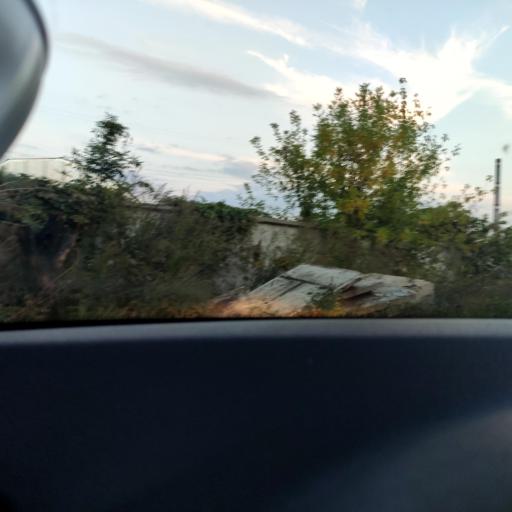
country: RU
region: Samara
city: Petra-Dubrava
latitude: 53.2607
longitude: 50.2856
